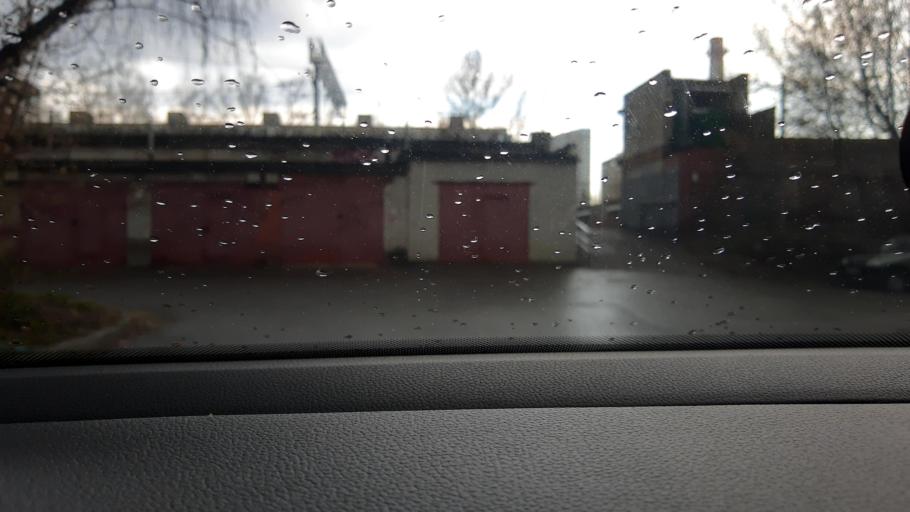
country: RU
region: Moskovskaya
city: Yubileyny
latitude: 55.9267
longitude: 37.8455
